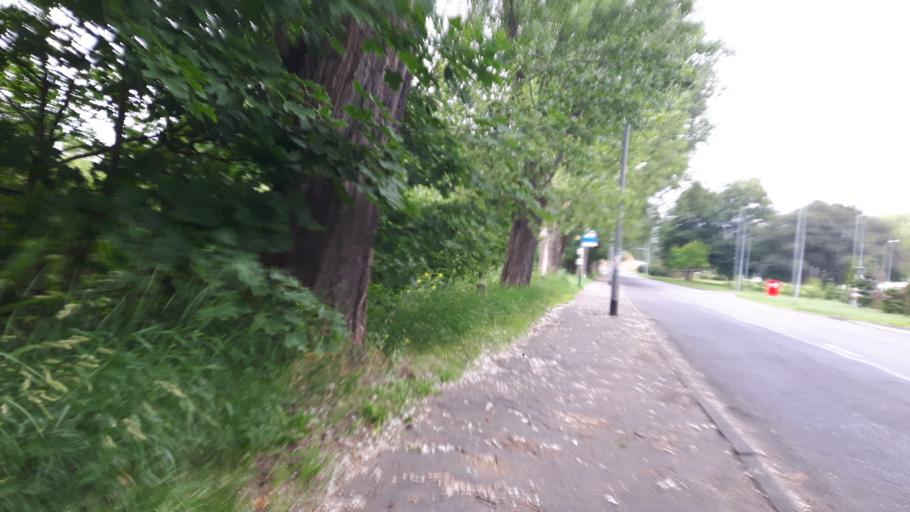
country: PL
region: West Pomeranian Voivodeship
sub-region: Szczecin
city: Szczecin
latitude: 53.3951
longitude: 14.6156
